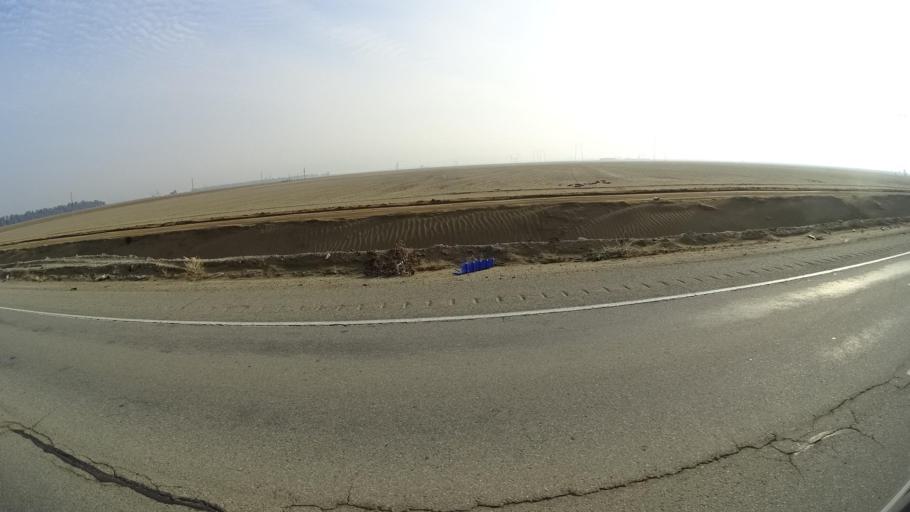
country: US
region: California
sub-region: Kern County
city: Weedpatch
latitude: 35.1278
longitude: -118.9147
